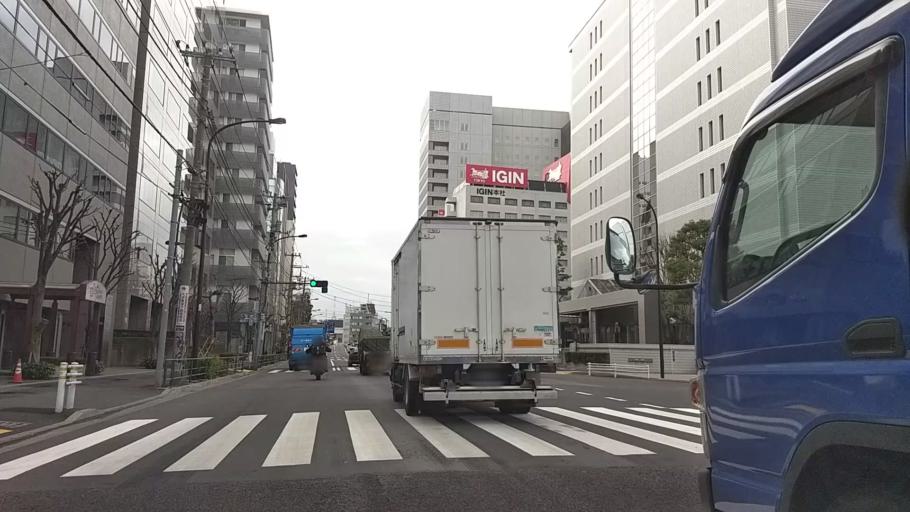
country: JP
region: Tokyo
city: Tokyo
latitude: 35.6257
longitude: 139.7450
